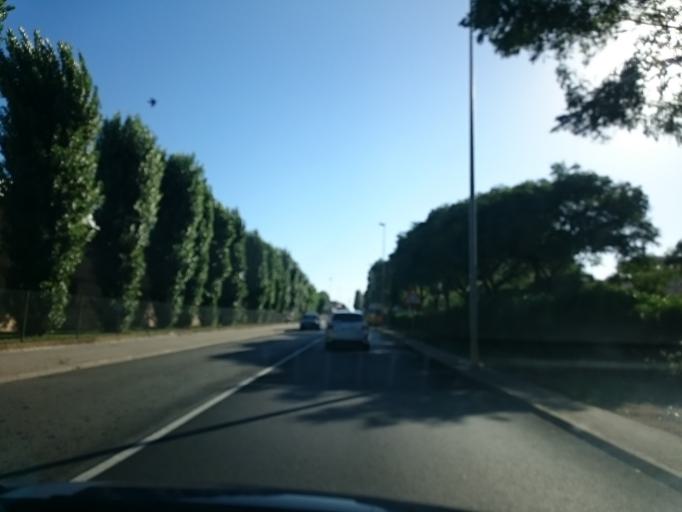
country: ES
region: Catalonia
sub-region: Provincia de Barcelona
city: Viladecans
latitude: 41.3093
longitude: 2.0142
